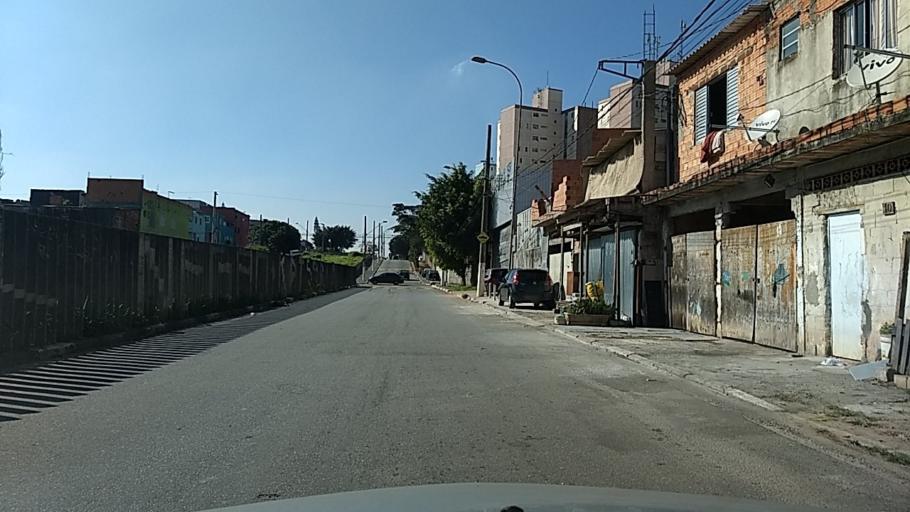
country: BR
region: Sao Paulo
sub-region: Osasco
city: Osasco
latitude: -23.5117
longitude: -46.7920
